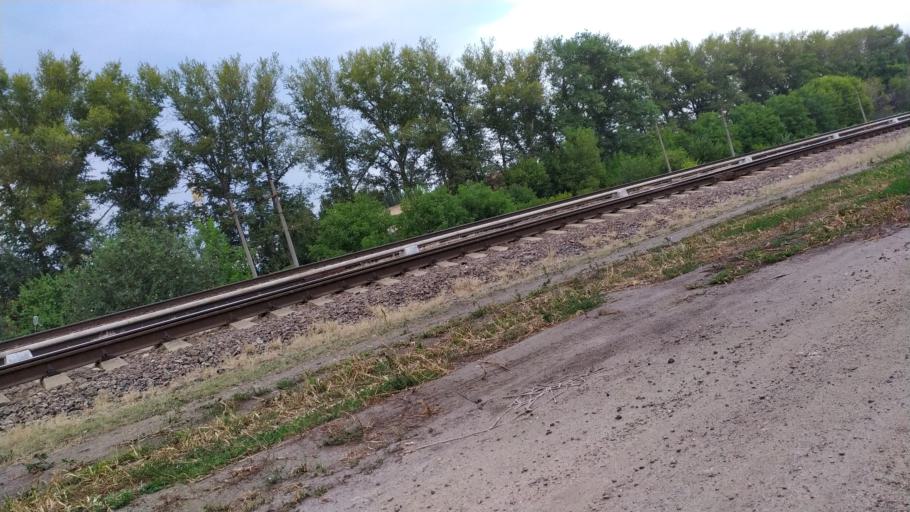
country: RU
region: Kursk
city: Kursk
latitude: 51.6562
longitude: 36.1427
